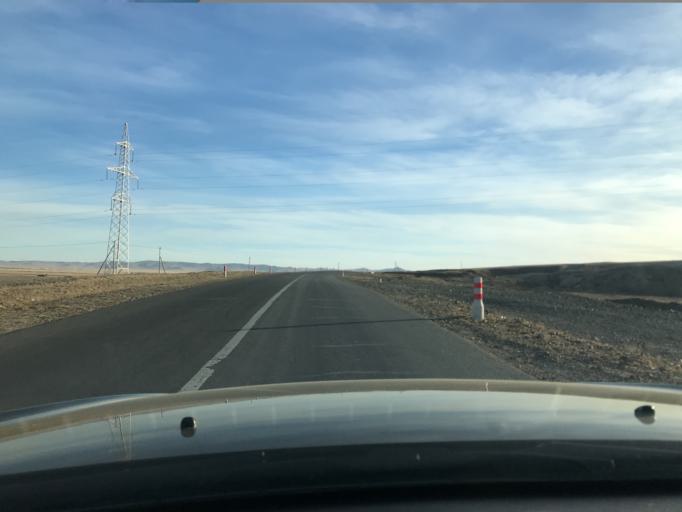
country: MN
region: Central Aimak
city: Dzuunmod
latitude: 47.7925
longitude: 107.3220
